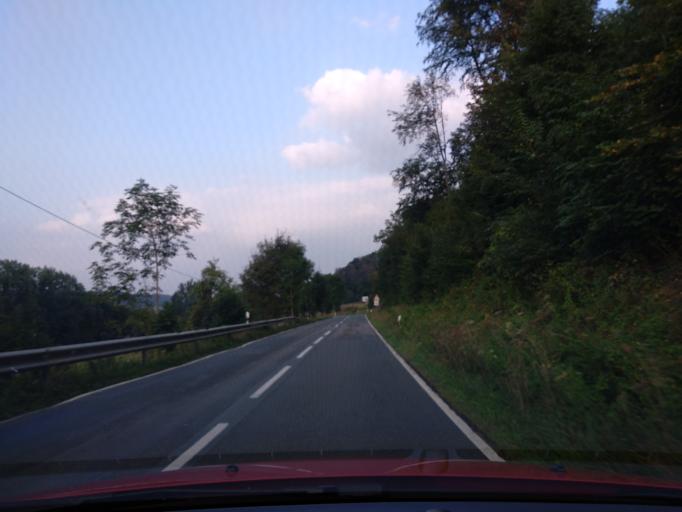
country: DE
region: North Rhine-Westphalia
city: Brakel
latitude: 51.6986
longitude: 9.2756
